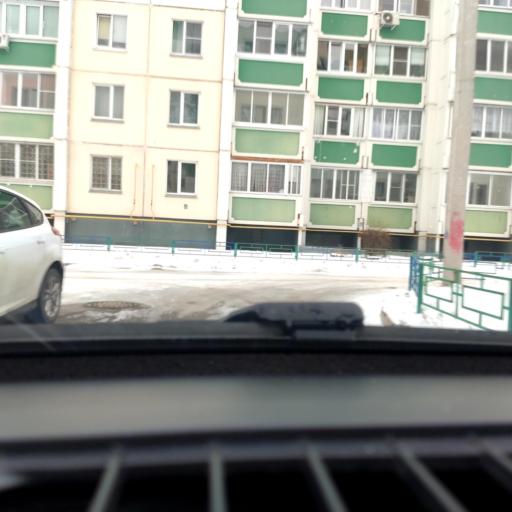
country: RU
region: Voronezj
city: Pridonskoy
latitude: 51.6263
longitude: 39.0674
